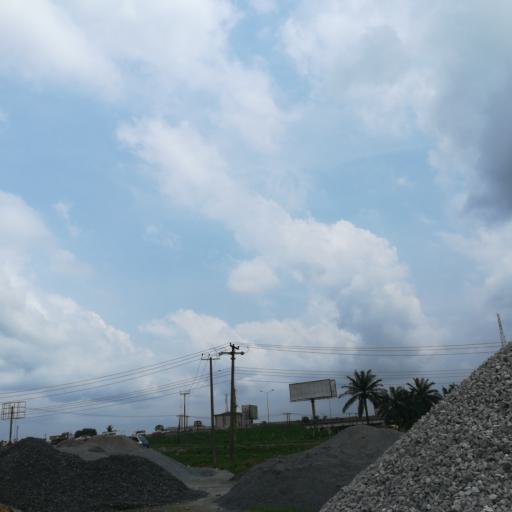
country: NG
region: Rivers
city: Port Harcourt
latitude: 4.8539
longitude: 7.0654
